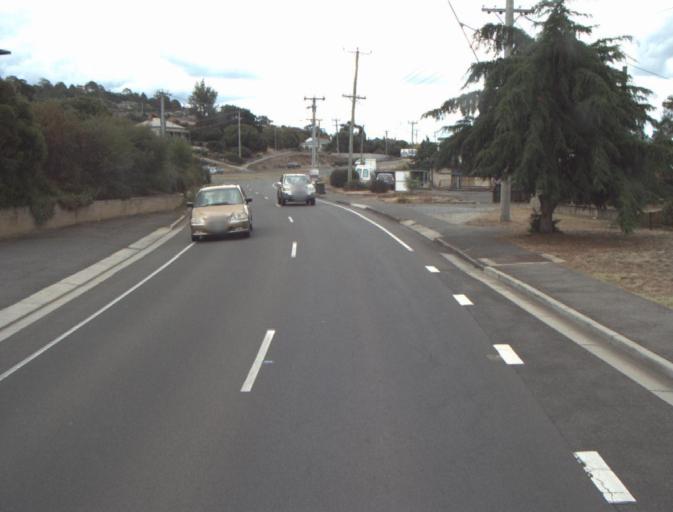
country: AU
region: Tasmania
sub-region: Launceston
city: Launceston
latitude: -41.4215
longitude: 147.1112
